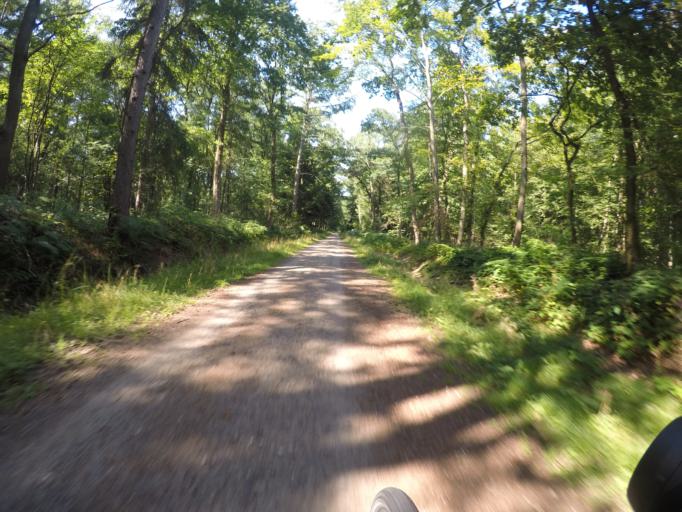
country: DE
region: Schleswig-Holstein
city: Glinde
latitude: 53.5150
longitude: 10.2154
